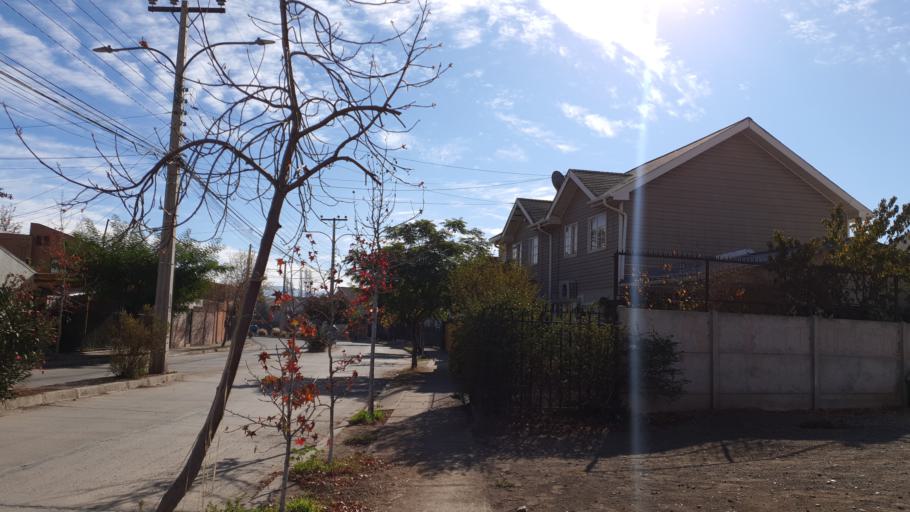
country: CL
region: Valparaiso
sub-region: Provincia de Los Andes
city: Los Andes
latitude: -32.8287
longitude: -70.5933
